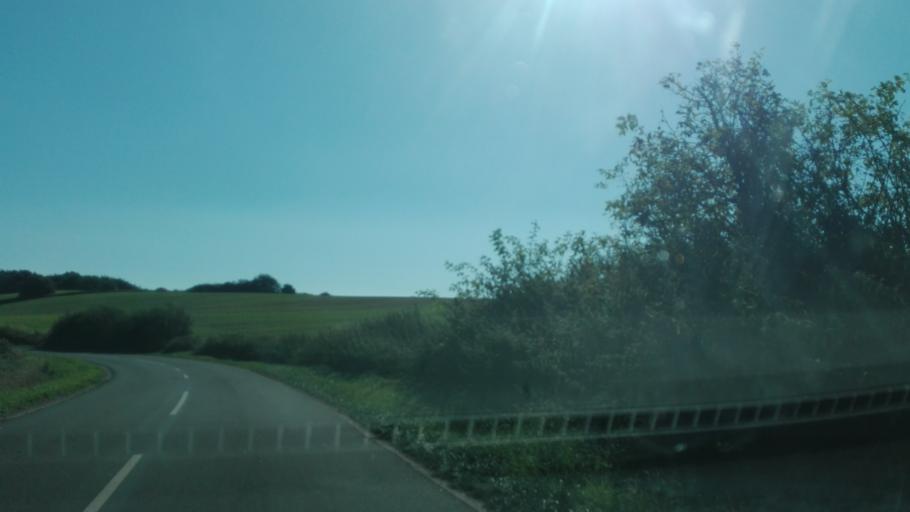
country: DK
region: Central Jutland
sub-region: Syddjurs Kommune
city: Ebeltoft
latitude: 56.2213
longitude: 10.7057
